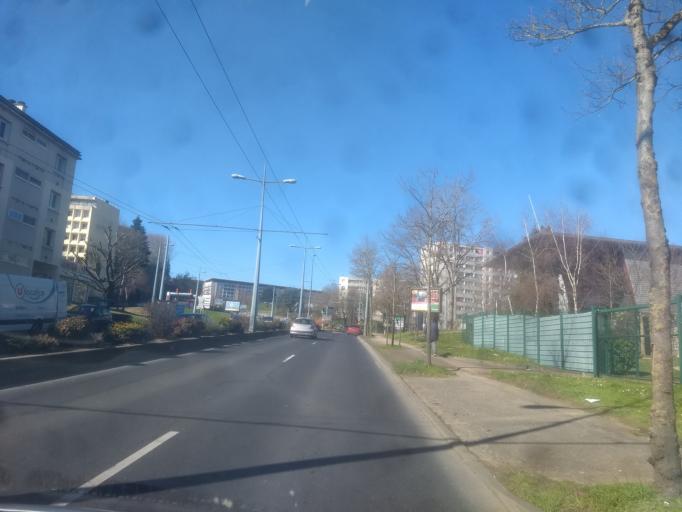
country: FR
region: Limousin
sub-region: Departement de la Haute-Vienne
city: Limoges
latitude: 45.8208
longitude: 1.2469
